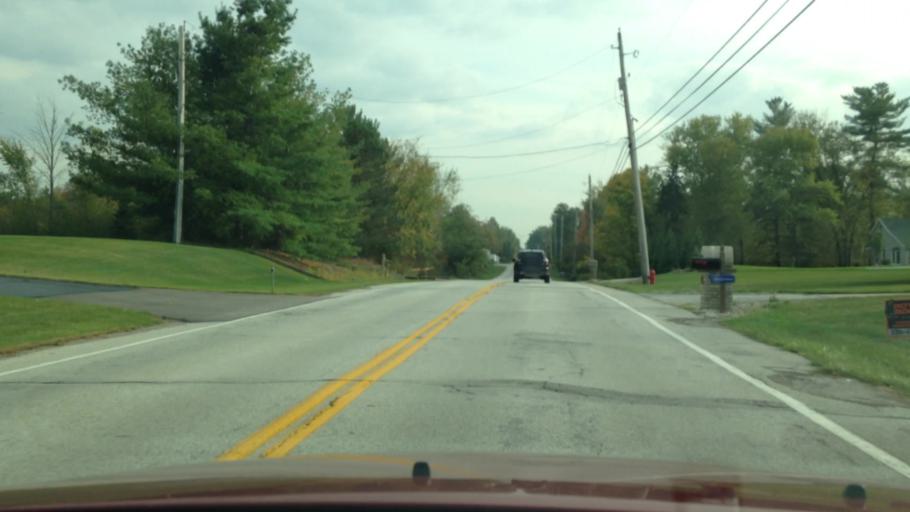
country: US
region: Ohio
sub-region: Cuyahoga County
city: Walton Hills
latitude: 41.3313
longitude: -81.5782
